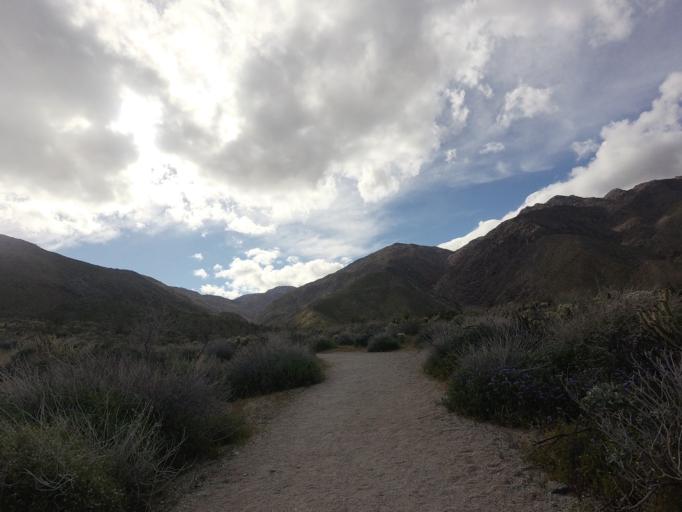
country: US
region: California
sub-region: San Diego County
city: Borrego Springs
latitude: 33.2446
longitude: -116.4165
